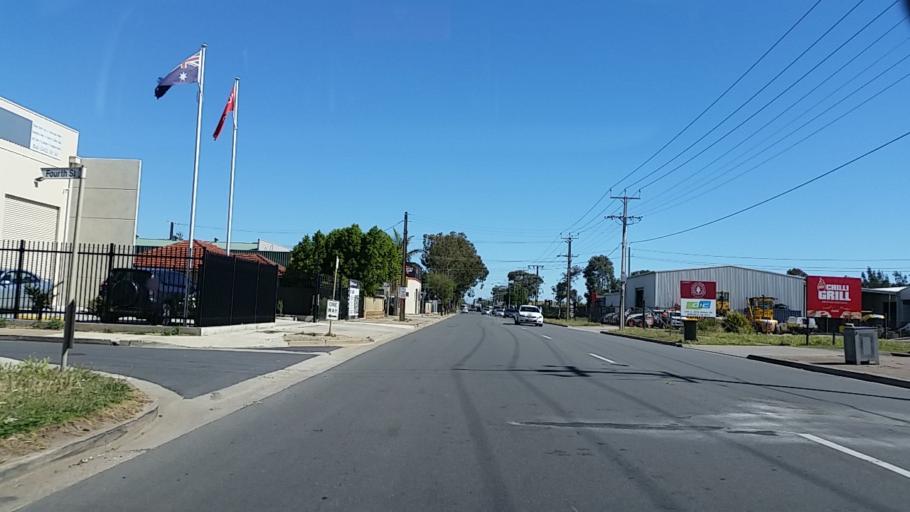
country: AU
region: South Australia
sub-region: Charles Sturt
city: Woodville North
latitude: -34.8477
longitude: 138.5466
